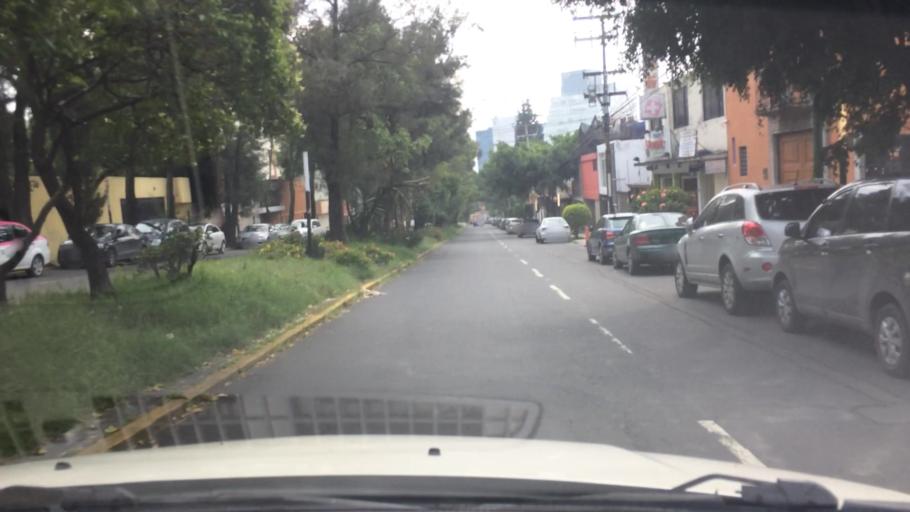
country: MX
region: Mexico City
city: Alvaro Obregon
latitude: 19.3579
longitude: -99.2021
